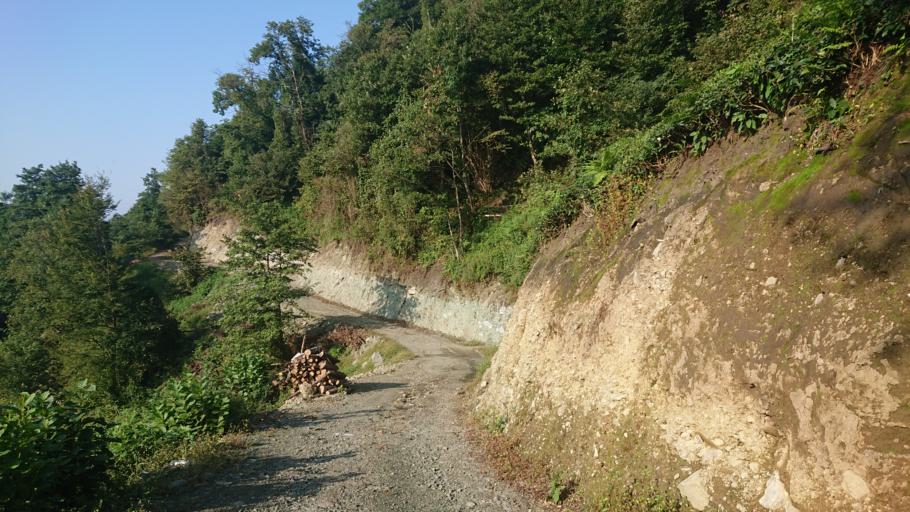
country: TR
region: Rize
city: Rize
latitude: 40.9860
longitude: 40.4983
